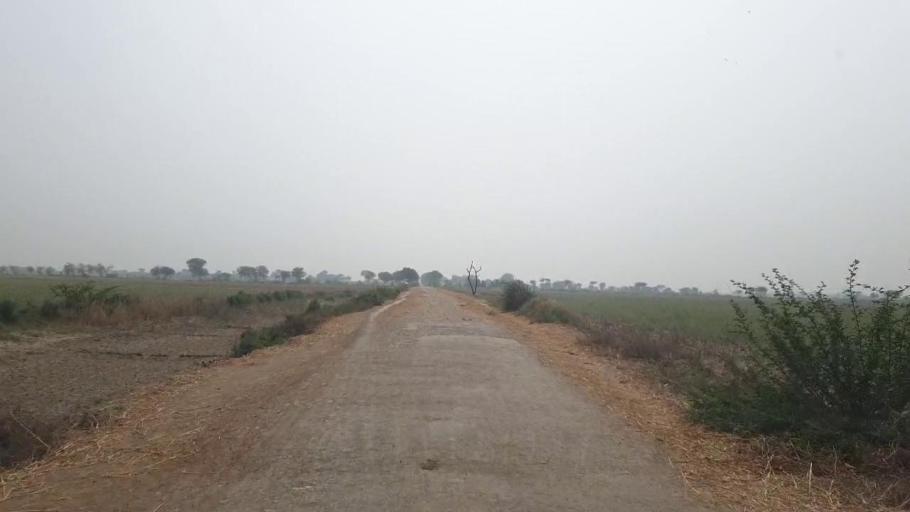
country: PK
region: Sindh
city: Kario
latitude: 24.6490
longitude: 68.6217
